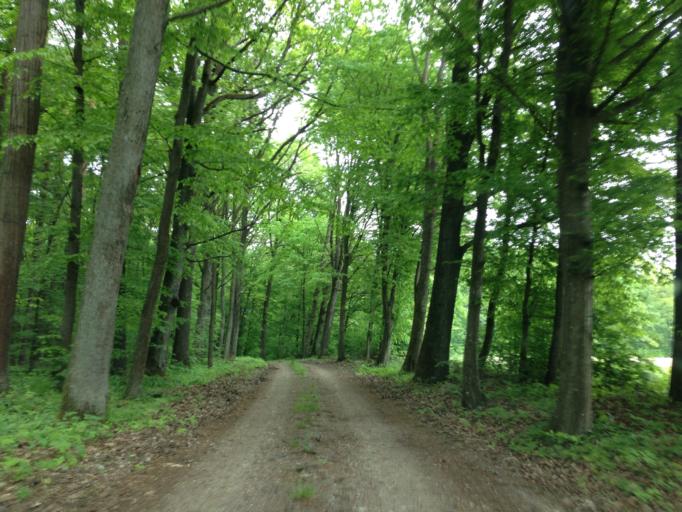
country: PL
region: Kujawsko-Pomorskie
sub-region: Powiat brodnicki
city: Gorzno
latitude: 53.2531
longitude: 19.7175
